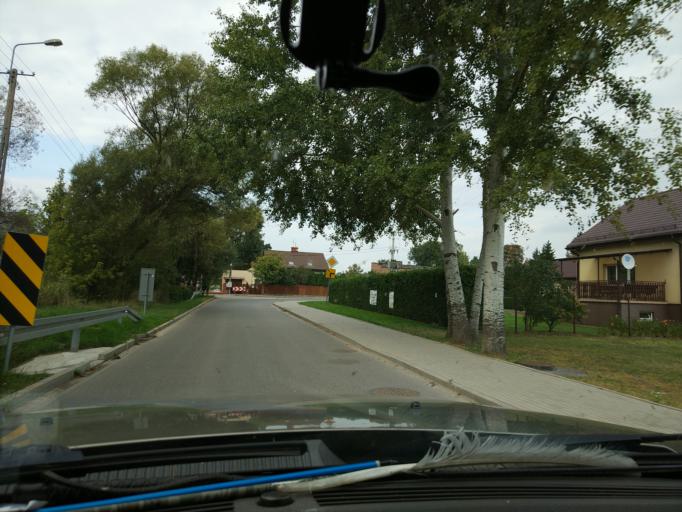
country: PL
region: Masovian Voivodeship
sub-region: Powiat pruszkowski
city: Otrebusy
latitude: 52.1276
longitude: 20.7502
